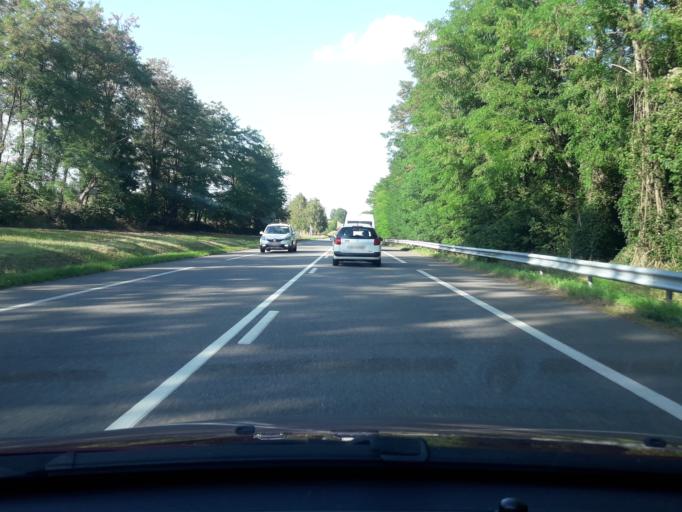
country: FR
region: Alsace
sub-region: Departement du Bas-Rhin
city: Wissembourg
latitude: 48.9946
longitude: 7.9646
